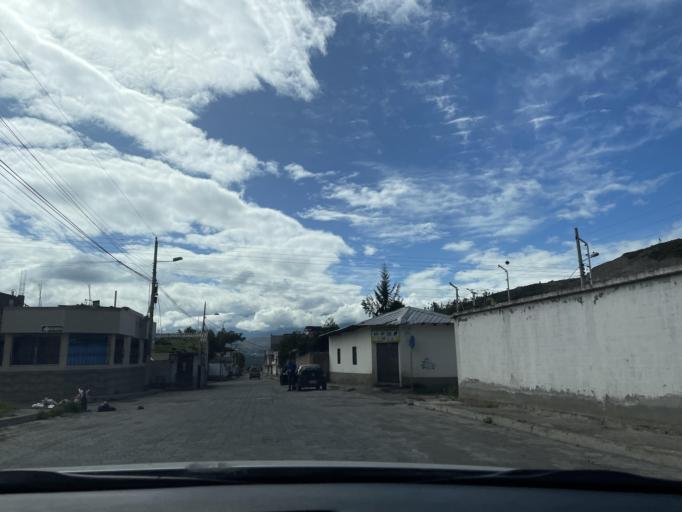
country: EC
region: Chimborazo
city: Guano
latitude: -1.6086
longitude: -78.6328
